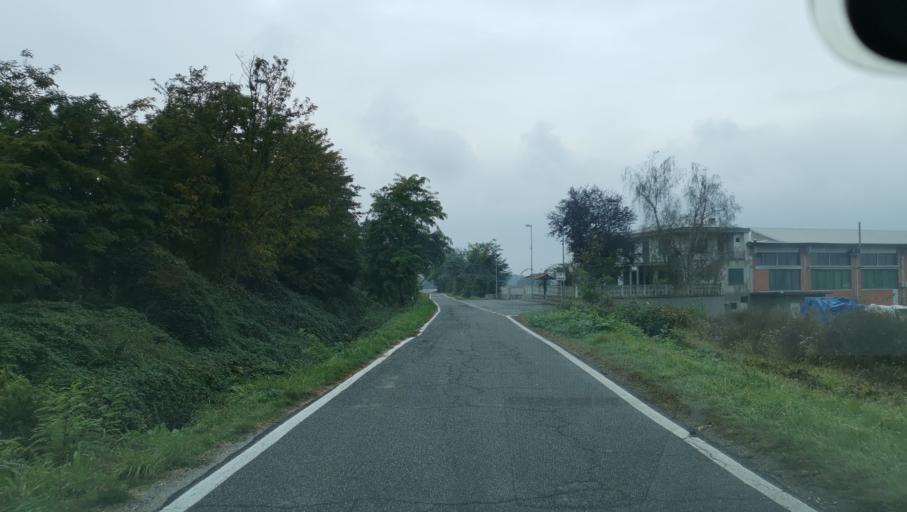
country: IT
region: Piedmont
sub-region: Provincia di Torino
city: San Raffaele Cimena
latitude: 45.1381
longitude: 7.8398
